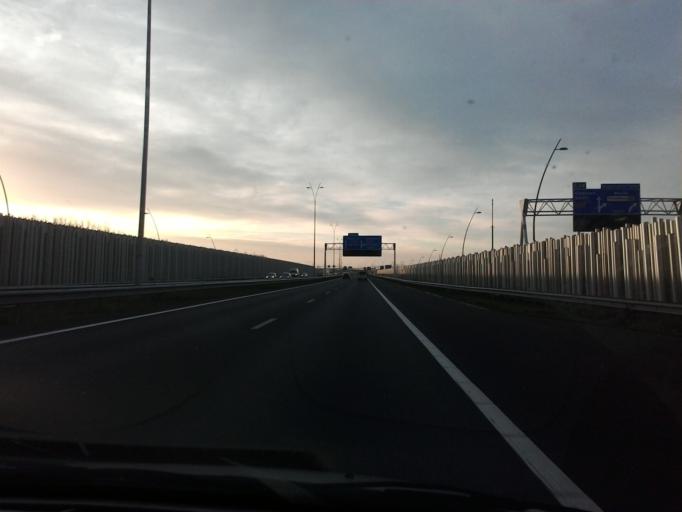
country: NL
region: North Brabant
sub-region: Gemeente Veldhoven
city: Veldhoven
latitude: 51.4168
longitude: 5.4290
